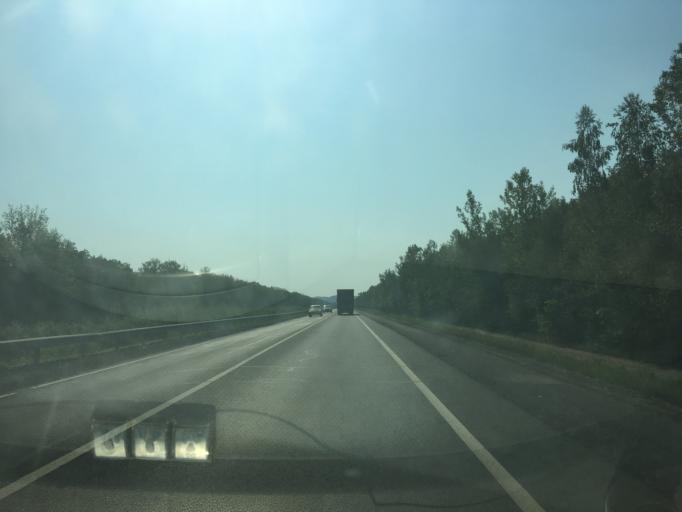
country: RU
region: Nizjnij Novgorod
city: Kstovo
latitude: 56.0892
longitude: 44.3356
